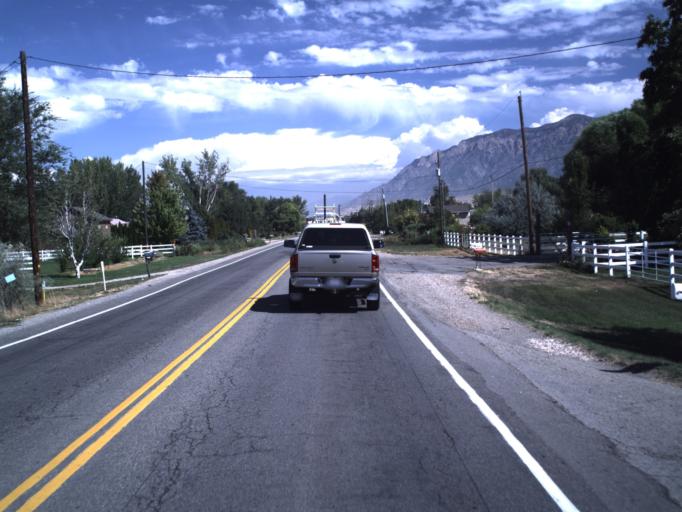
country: US
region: Utah
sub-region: Weber County
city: Marriott-Slaterville
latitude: 41.2491
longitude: -112.0252
